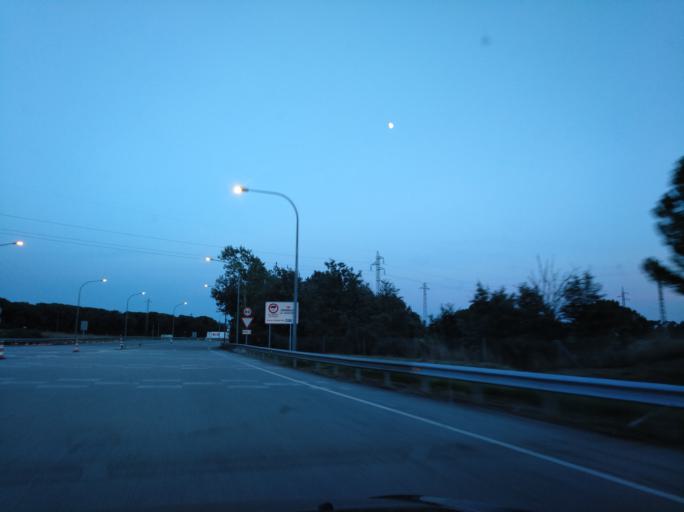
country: ES
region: Catalonia
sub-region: Provincia de Girona
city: Riudellots de la Selva
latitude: 41.8951
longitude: 2.7779
